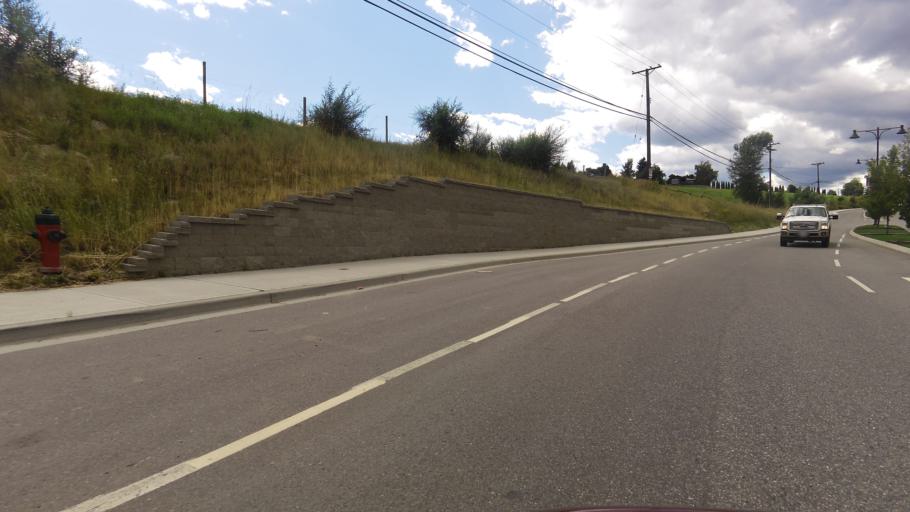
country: CA
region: British Columbia
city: West Kelowna
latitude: 49.8726
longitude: -119.5443
